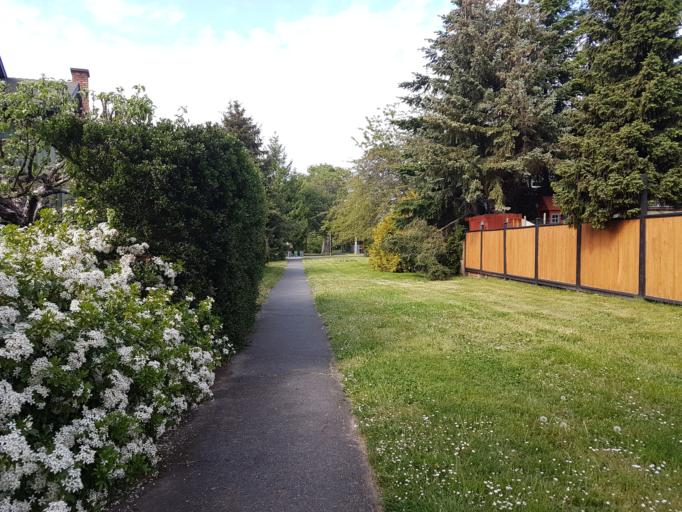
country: CA
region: British Columbia
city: Oak Bay
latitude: 48.4861
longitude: -123.3346
